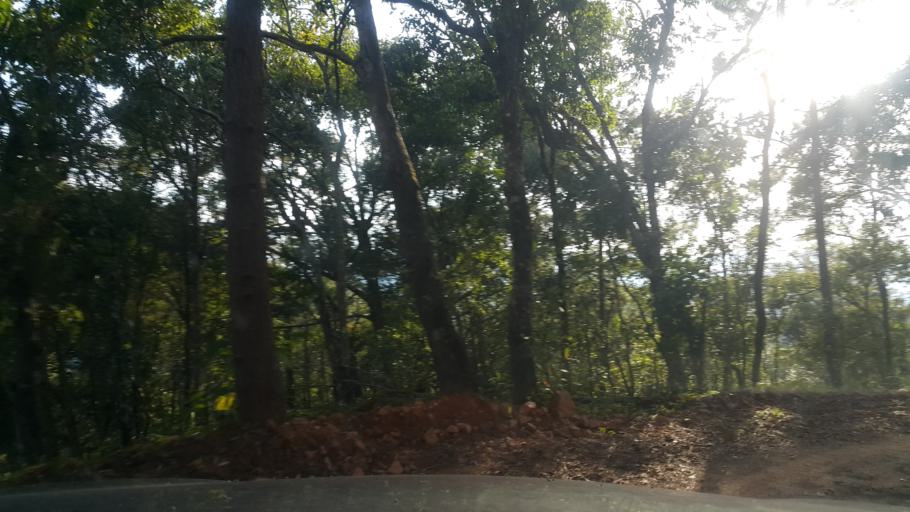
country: TH
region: Chiang Mai
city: Samoeng
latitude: 19.0285
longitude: 98.6472
